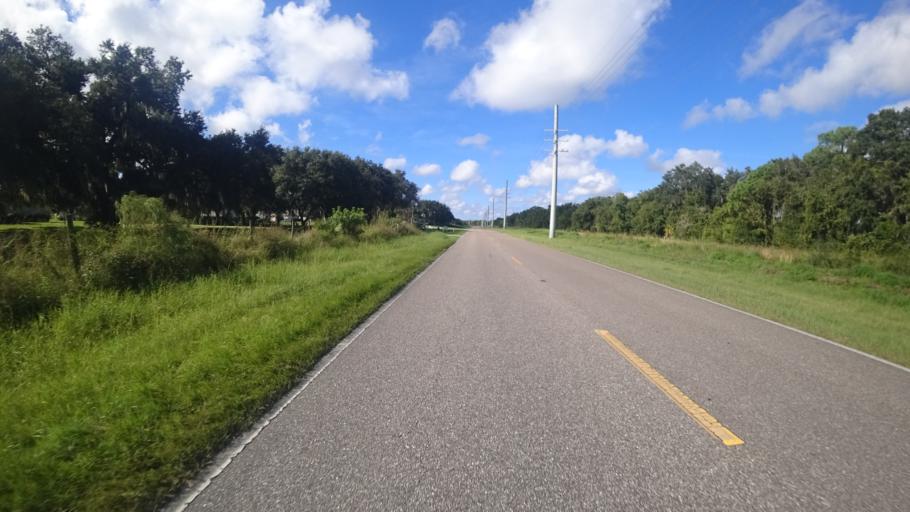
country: US
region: Florida
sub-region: Manatee County
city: Ellenton
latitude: 27.5742
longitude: -82.4716
